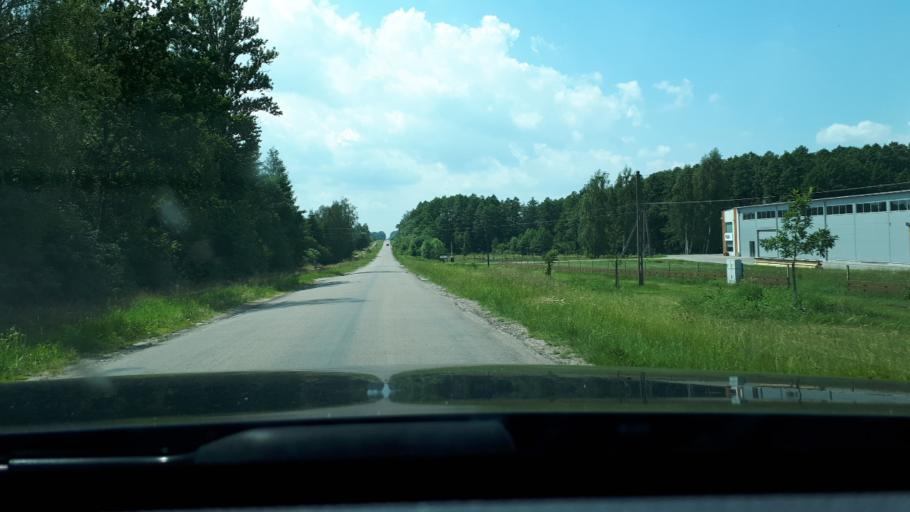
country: PL
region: Podlasie
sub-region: Powiat bialostocki
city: Choroszcz
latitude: 53.1243
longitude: 22.9500
